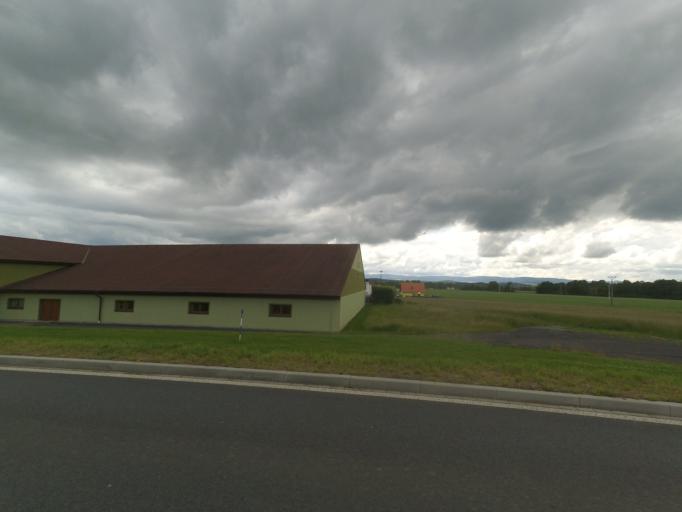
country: CZ
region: Plzensky
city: Horsovsky Tyn
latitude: 49.5344
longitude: 12.9285
